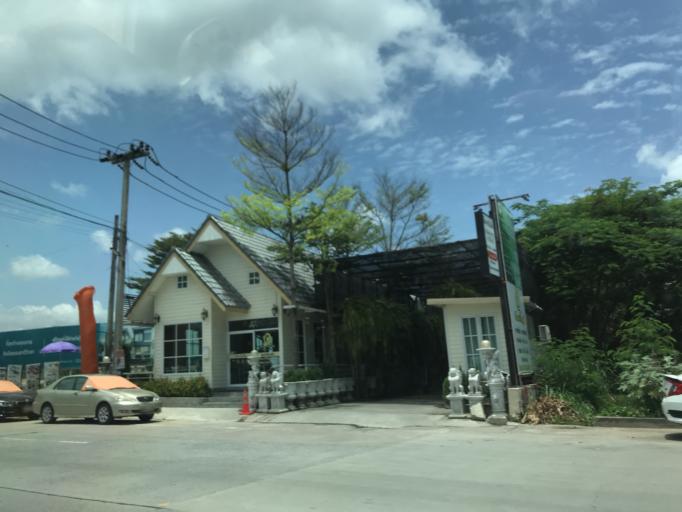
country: TH
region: Chon Buri
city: Si Racha
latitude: 13.1465
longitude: 100.9824
